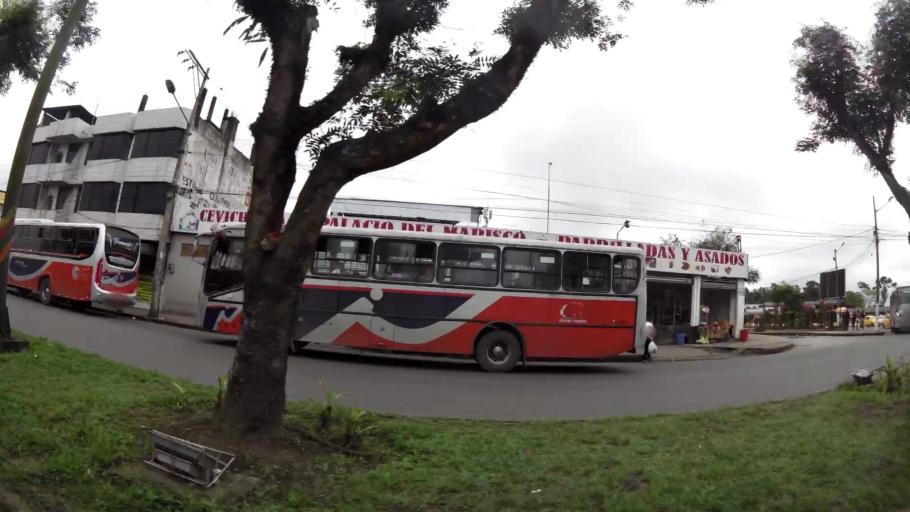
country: EC
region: Santo Domingo de los Tsachilas
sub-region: Canton Santo Domingo de los Colorados
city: Santo Domingo de los Colorados
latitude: -0.2402
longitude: -79.1695
